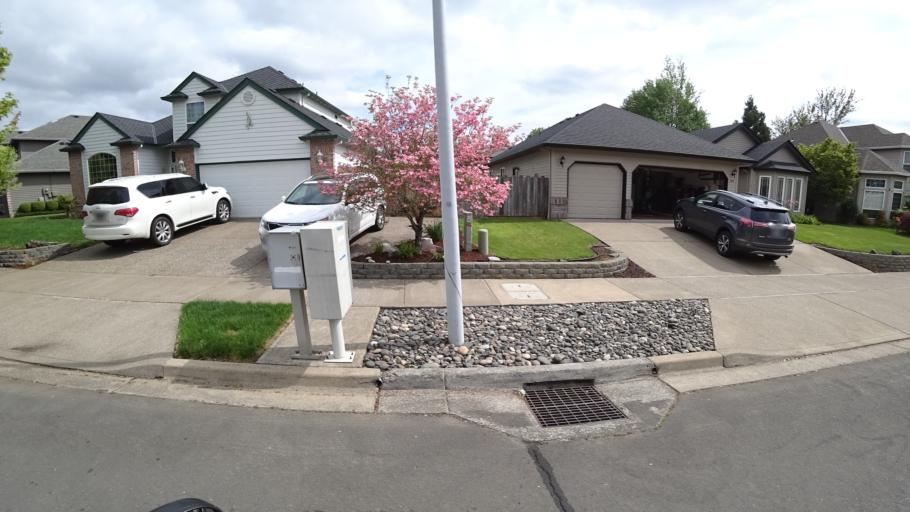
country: US
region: Oregon
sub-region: Washington County
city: Hillsboro
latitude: 45.5475
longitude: -122.9877
